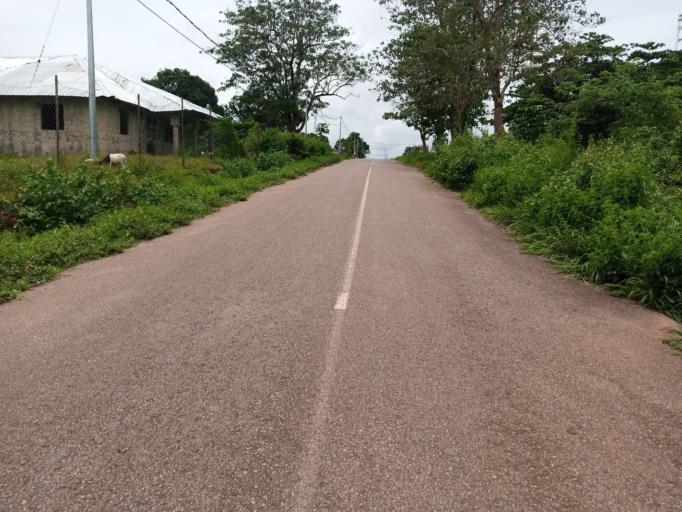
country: SL
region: Southern Province
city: Largo
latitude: 8.2027
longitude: -12.0623
